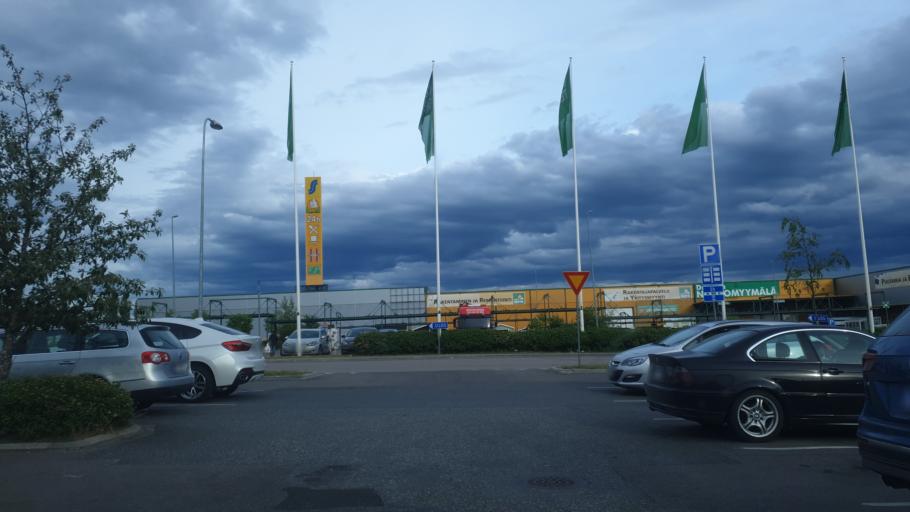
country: FI
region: Paijanne Tavastia
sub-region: Lahti
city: Lahti
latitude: 60.9346
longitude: 25.6351
